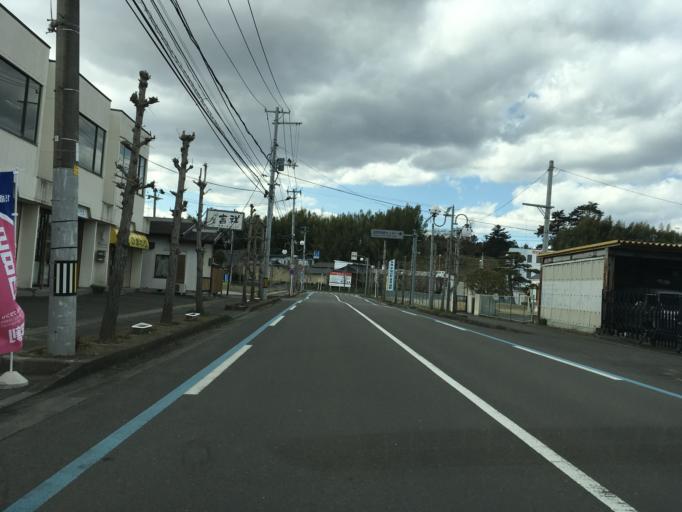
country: JP
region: Miyagi
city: Wakuya
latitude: 38.6912
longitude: 141.1871
